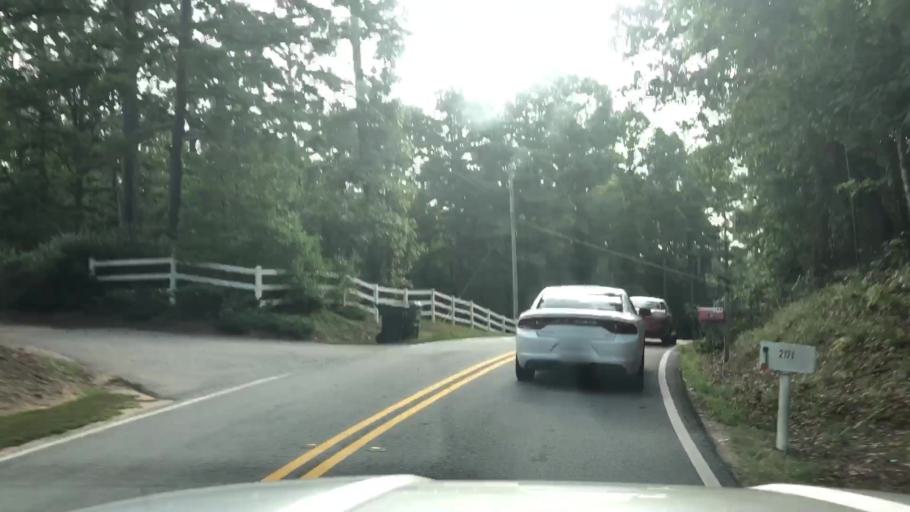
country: US
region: Georgia
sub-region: Bartow County
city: Euharlee
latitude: 34.0471
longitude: -84.8603
